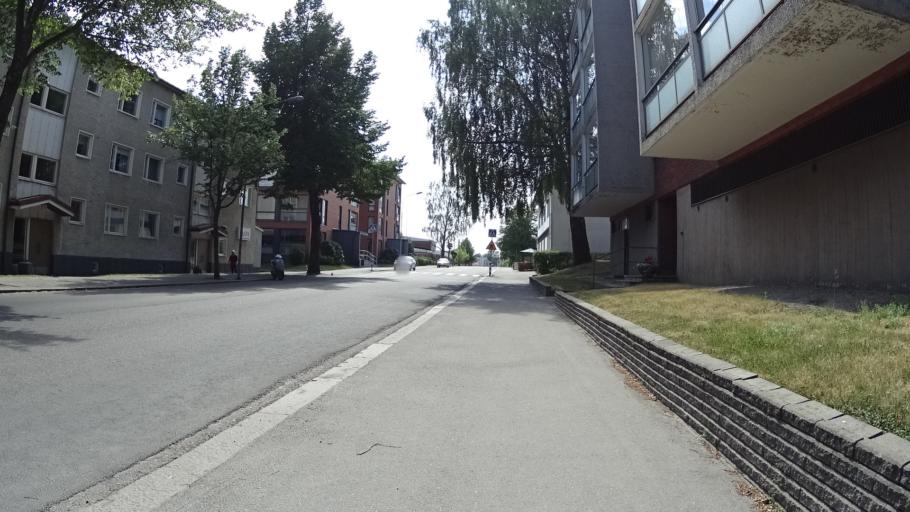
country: FI
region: Uusimaa
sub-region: Raaseporin
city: Karis
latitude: 60.0727
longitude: 23.6664
